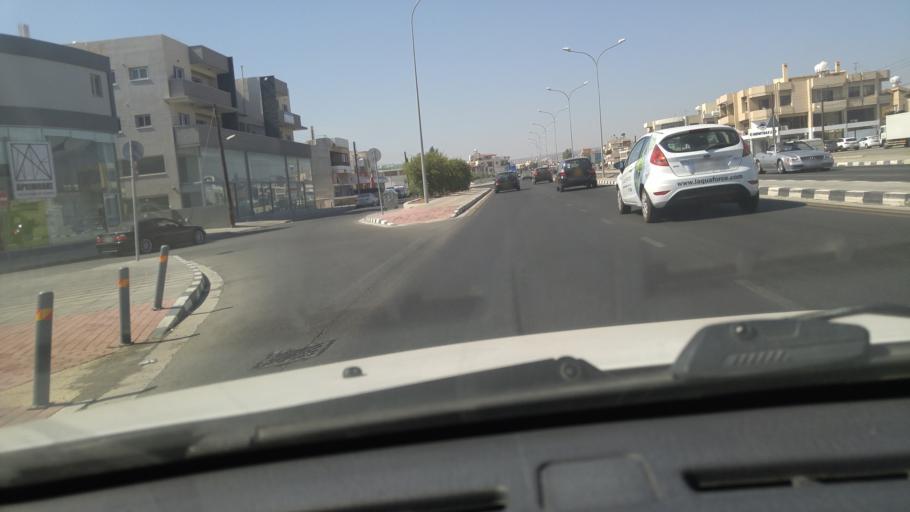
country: CY
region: Limassol
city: Pano Polemidia
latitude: 34.6785
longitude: 32.9957
